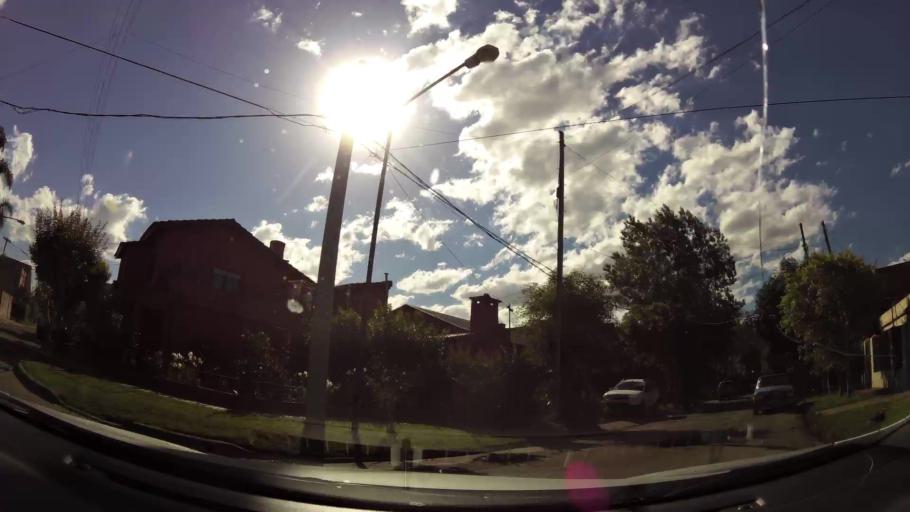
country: AR
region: Buenos Aires
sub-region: Partido de Tigre
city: Tigre
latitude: -34.4728
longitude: -58.5599
